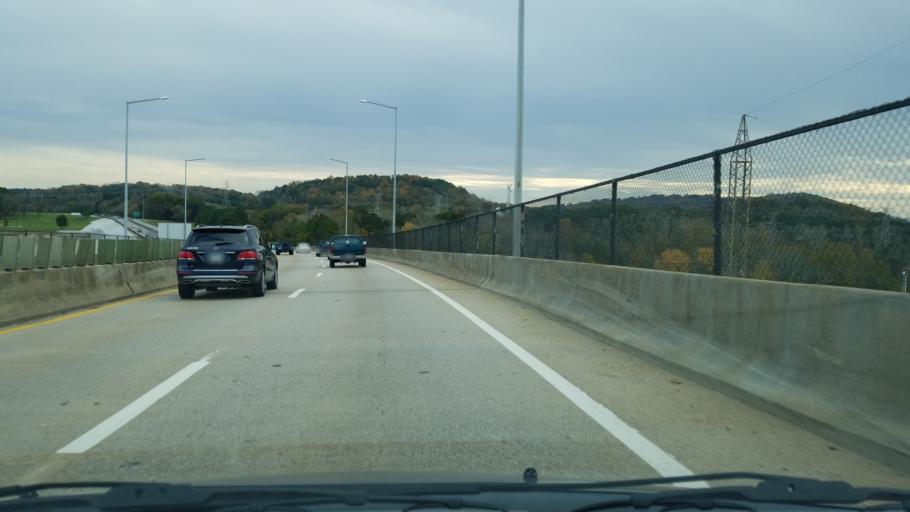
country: US
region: Tennessee
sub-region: Hamilton County
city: East Chattanooga
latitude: 35.1010
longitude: -85.2290
